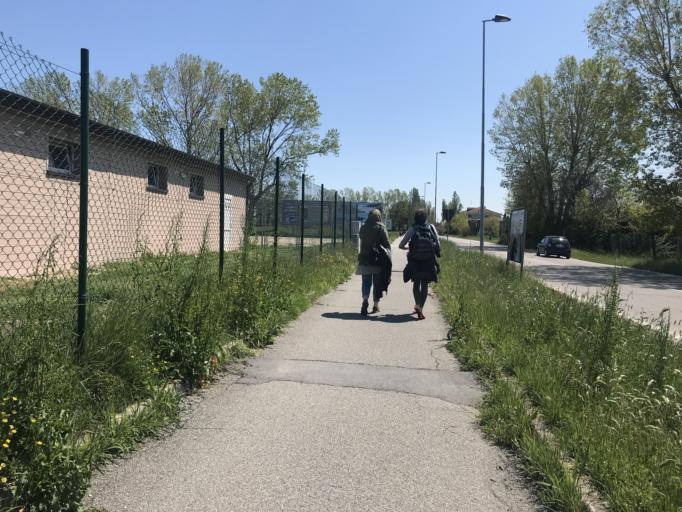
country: IT
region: Emilia-Romagna
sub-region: Provincia di Rimini
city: Rimini
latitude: 44.0749
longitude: 12.5488
